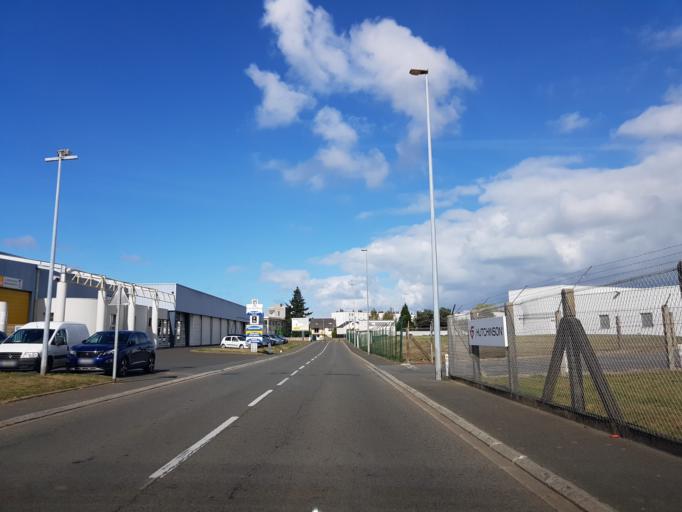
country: FR
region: Brittany
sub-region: Departement des Cotes-d'Armor
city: Langueux
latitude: 48.5066
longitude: -2.7403
